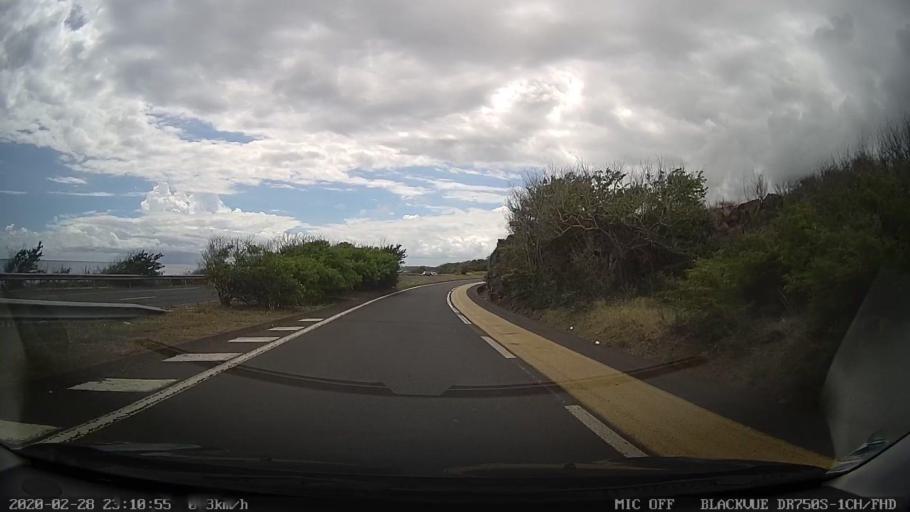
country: RE
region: Reunion
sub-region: Reunion
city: Trois-Bassins
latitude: -21.1146
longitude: 55.2568
